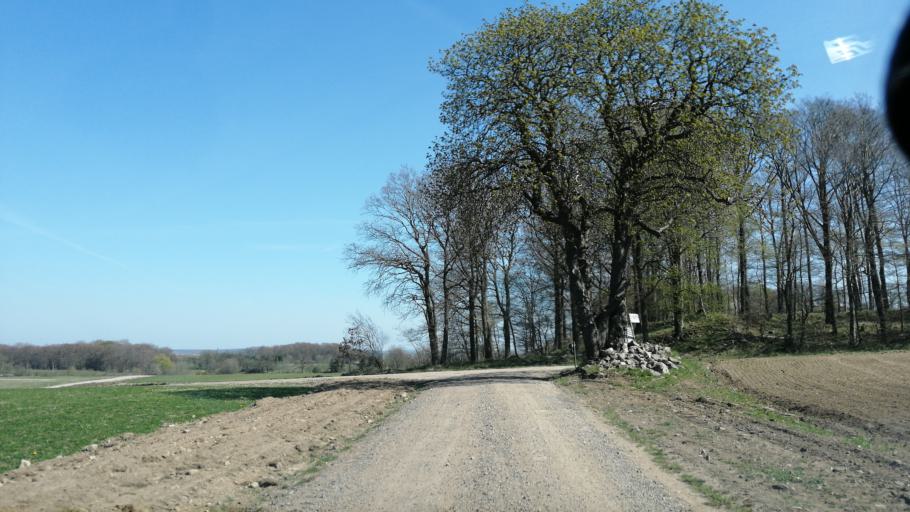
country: SE
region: Skane
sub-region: Astorps Kommun
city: Kvidinge
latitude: 56.1033
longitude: 13.0814
